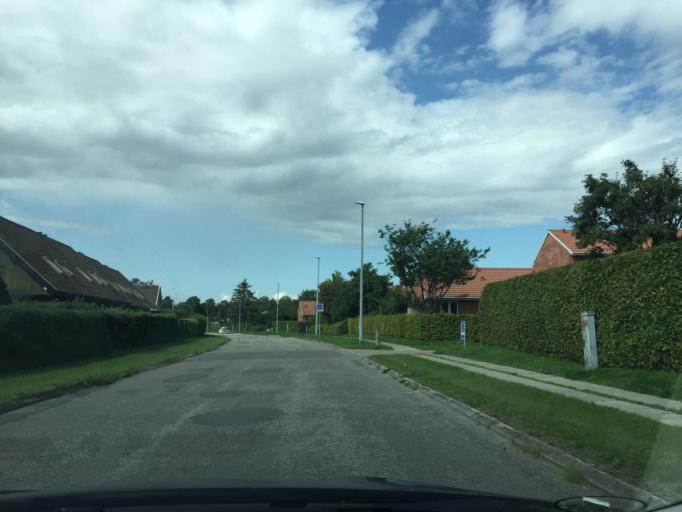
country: DK
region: South Denmark
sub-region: Odense Kommune
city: Neder Holluf
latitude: 55.3643
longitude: 10.4564
